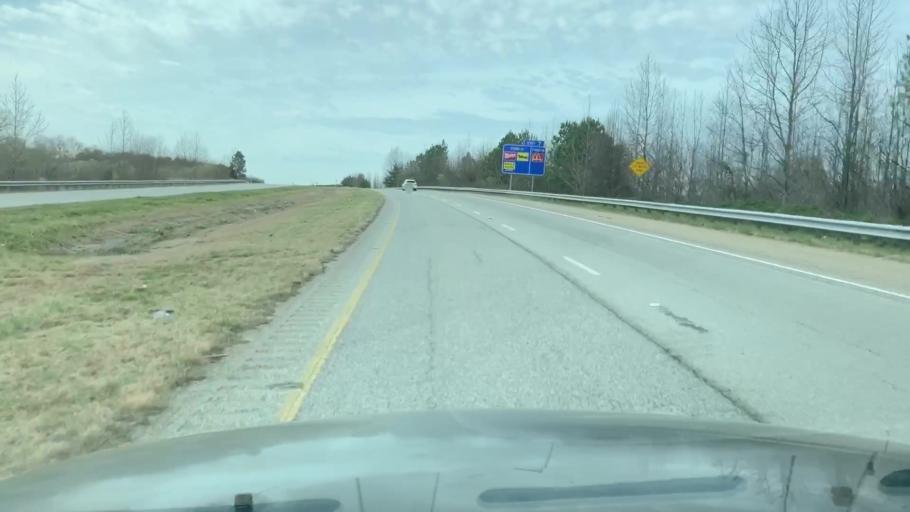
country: US
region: South Carolina
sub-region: Greenville County
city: Golden Grove
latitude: 34.7233
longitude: -82.3766
